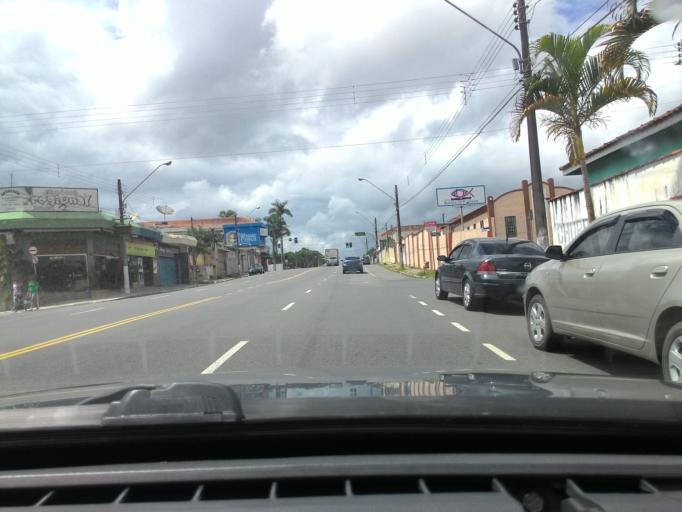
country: BR
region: Sao Paulo
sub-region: Registro
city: Registro
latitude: -24.5032
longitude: -47.8410
